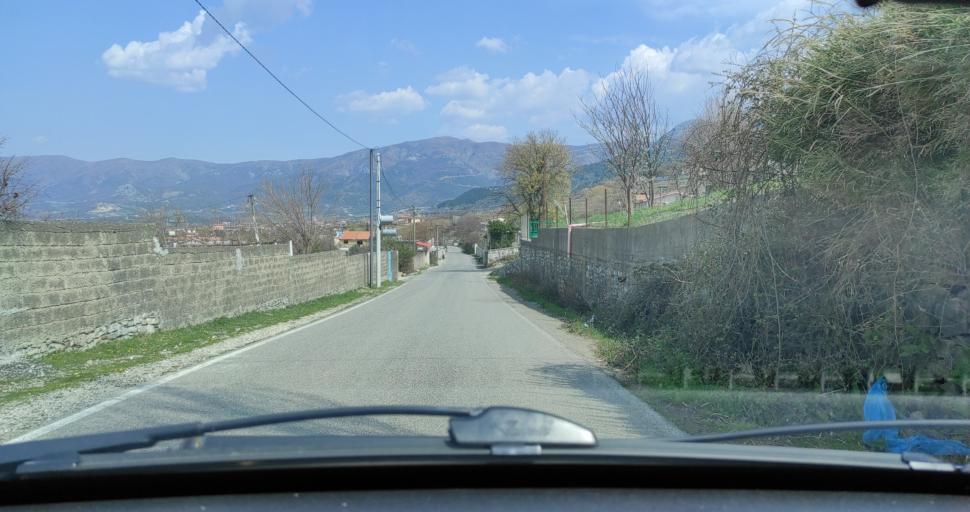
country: AL
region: Lezhe
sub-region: Rrethi i Lezhes
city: Kallmeti i Madh
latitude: 41.8424
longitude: 19.6788
